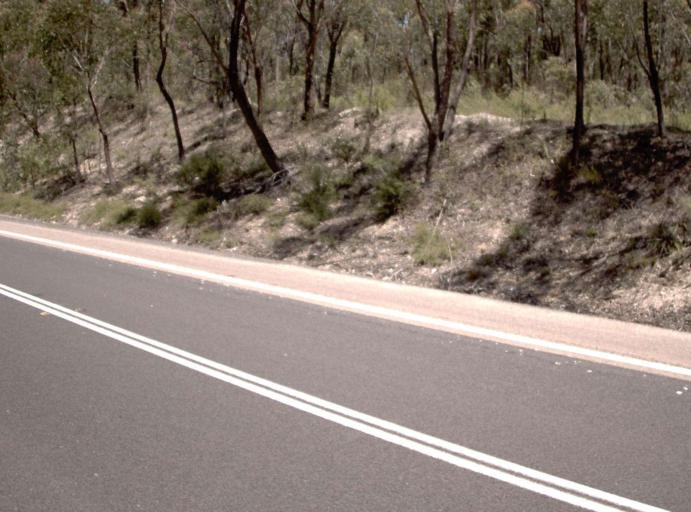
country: AU
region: Victoria
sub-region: East Gippsland
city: Lakes Entrance
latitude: -37.7005
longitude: 148.6027
